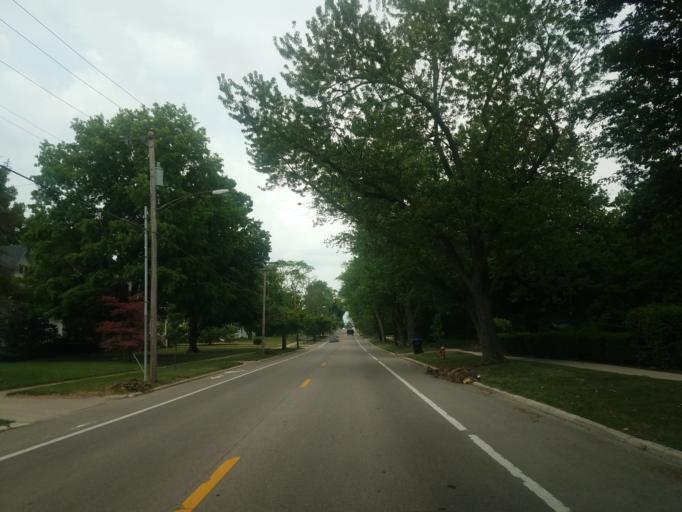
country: US
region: Illinois
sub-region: McLean County
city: Bloomington
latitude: 40.4800
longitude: -88.9697
